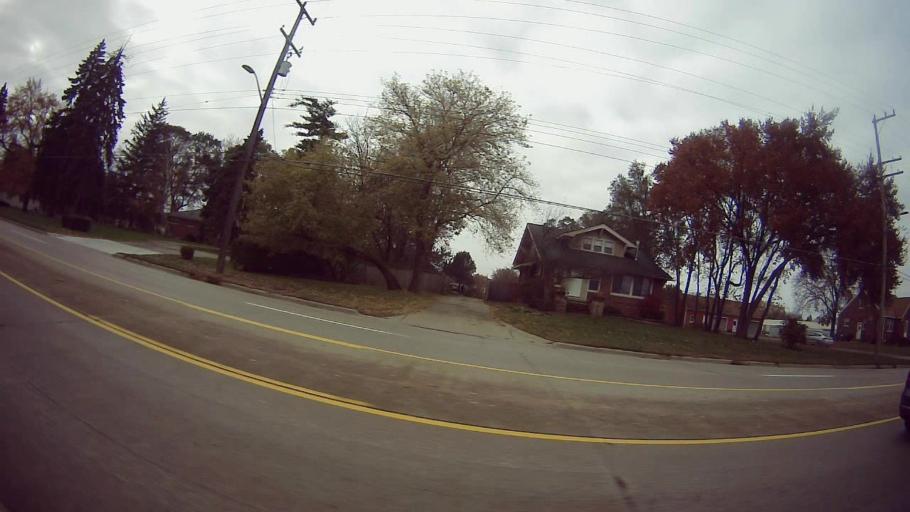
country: US
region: Michigan
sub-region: Oakland County
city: Madison Heights
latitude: 42.4976
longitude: -83.0671
